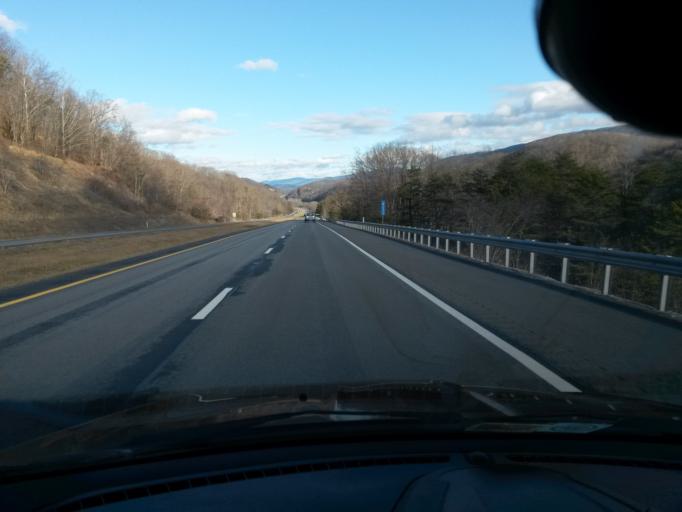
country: US
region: West Virginia
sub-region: Mercer County
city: Athens
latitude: 37.3453
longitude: -80.9319
